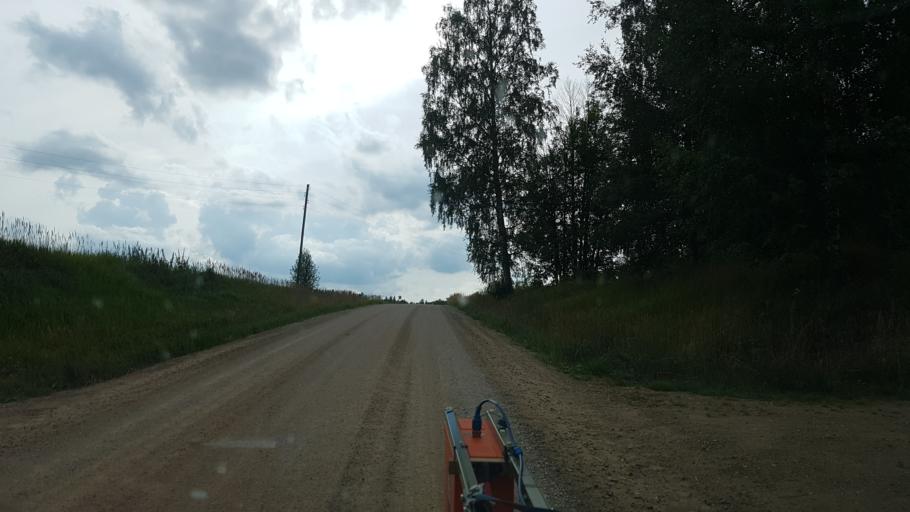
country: RU
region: Pskov
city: Pechory
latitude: 57.7751
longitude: 27.4621
